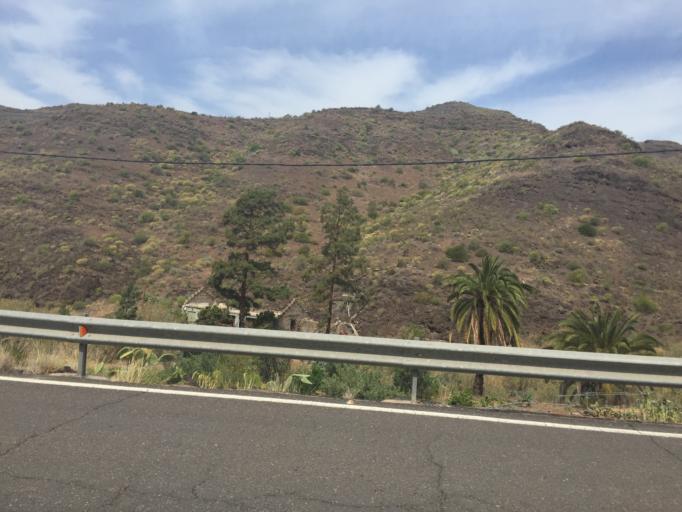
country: ES
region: Canary Islands
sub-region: Provincia de Las Palmas
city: Mogan
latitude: 27.8928
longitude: -15.7156
